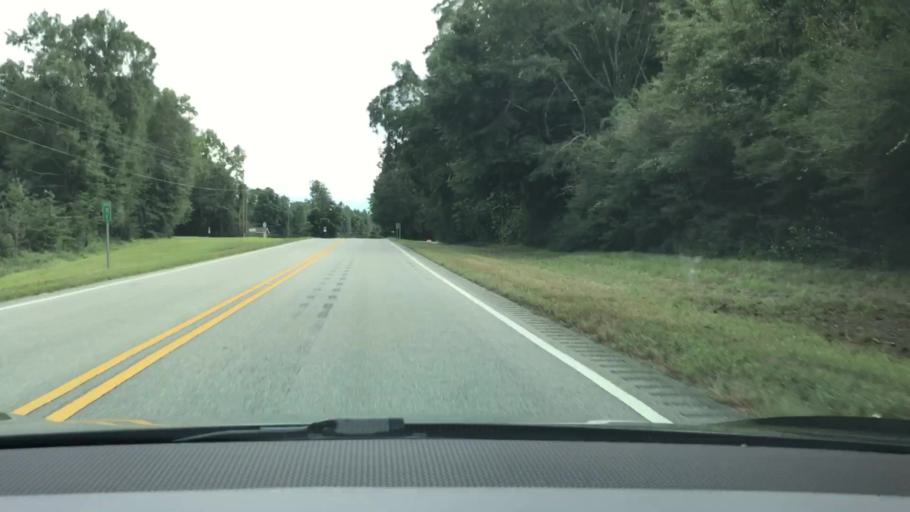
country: US
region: Alabama
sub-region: Pike County
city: Troy
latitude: 31.6378
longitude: -85.9721
